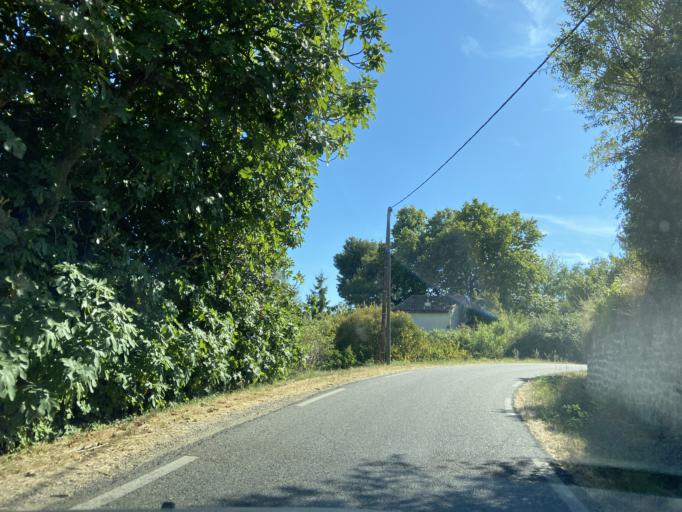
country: FR
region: Provence-Alpes-Cote d'Azur
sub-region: Departement des Bouches-du-Rhone
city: Saint-Chamas
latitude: 43.5607
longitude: 5.0261
